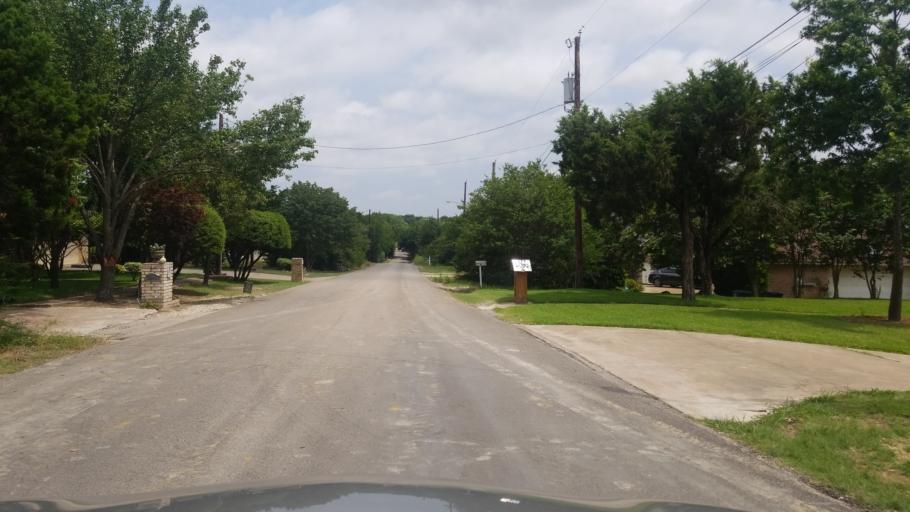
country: US
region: Texas
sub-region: Dallas County
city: Duncanville
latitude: 32.6783
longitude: -96.9327
